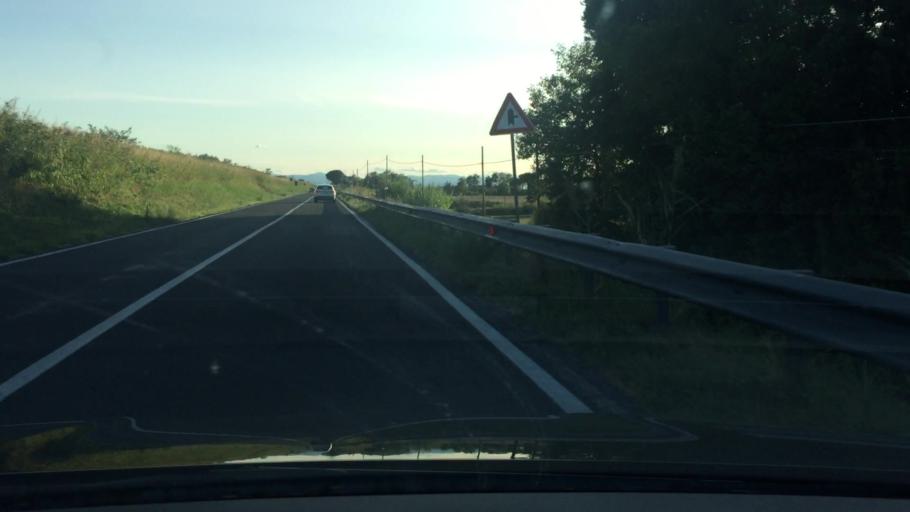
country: IT
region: Emilia-Romagna
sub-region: Provincia di Ravenna
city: Savio
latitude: 44.3011
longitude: 12.2819
